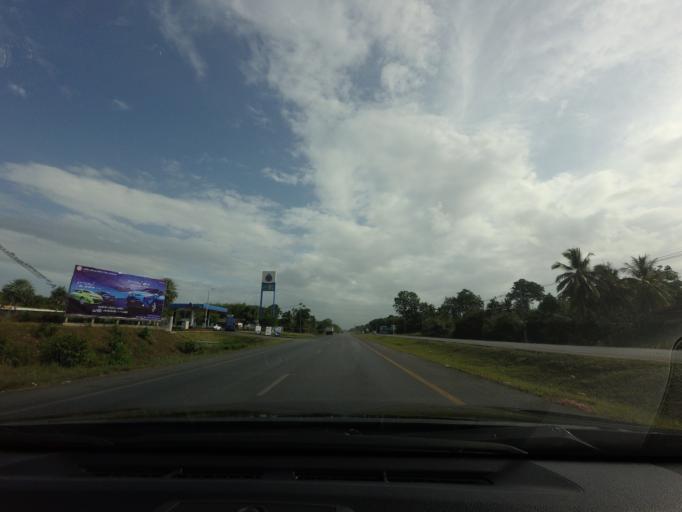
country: TH
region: Yala
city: Yala
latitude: 6.5601
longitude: 101.2610
